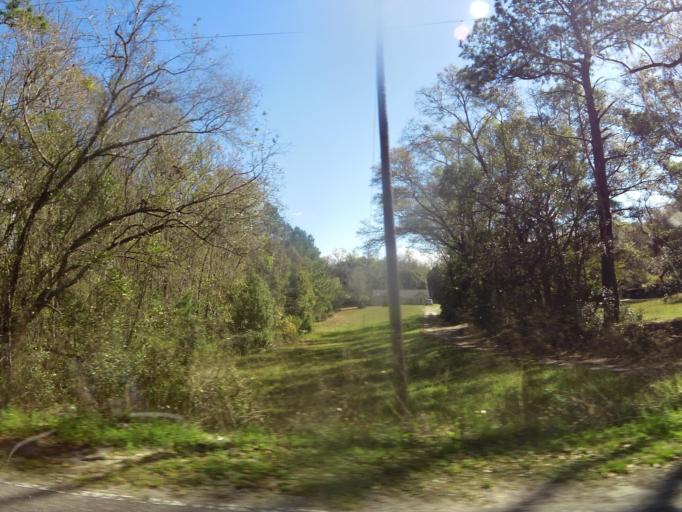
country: US
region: Florida
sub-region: Clay County
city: Green Cove Springs
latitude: 29.9807
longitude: -81.7059
